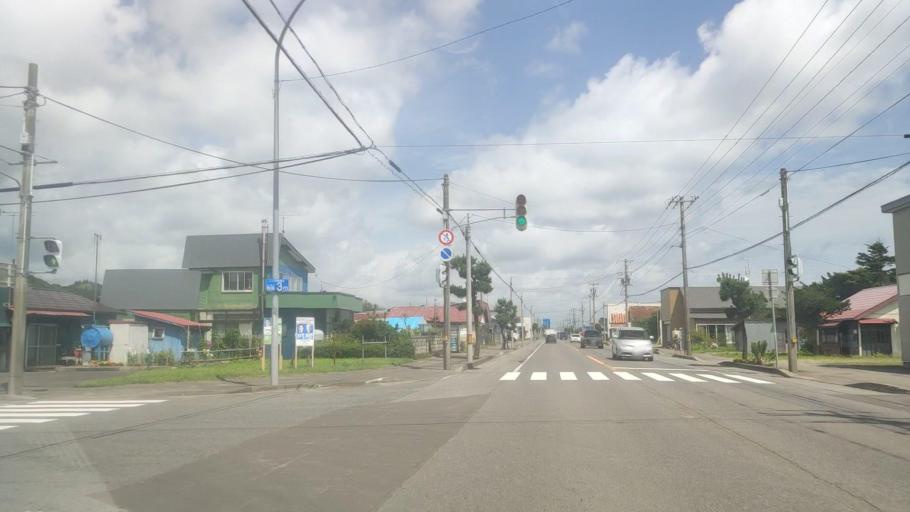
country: JP
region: Hokkaido
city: Niseko Town
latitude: 42.4360
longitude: 140.3215
